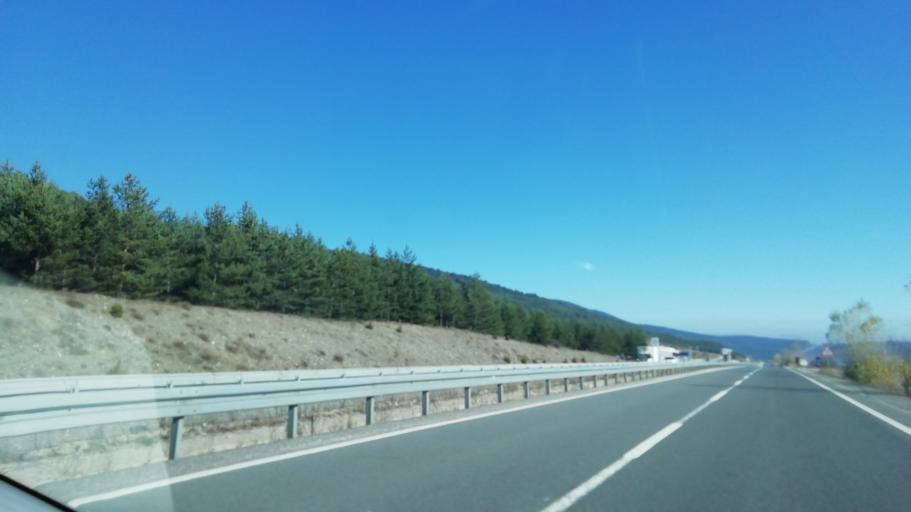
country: TR
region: Bolu
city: Gerede
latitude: 40.8239
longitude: 32.3355
